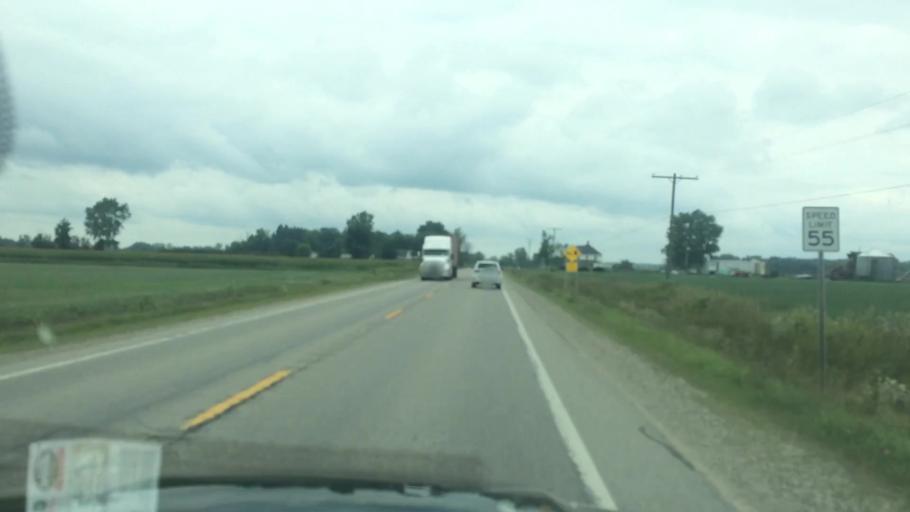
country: US
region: Michigan
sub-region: Tuscola County
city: Cass City
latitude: 43.5168
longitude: -83.0926
